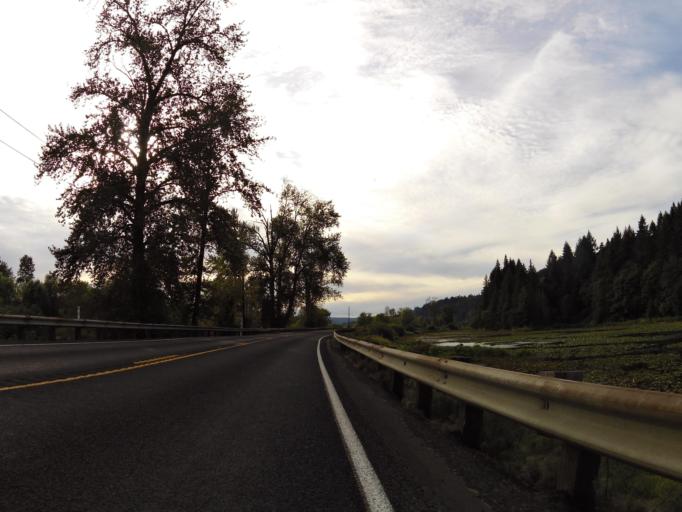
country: US
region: Washington
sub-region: Cowlitz County
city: West Longview
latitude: 46.1830
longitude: -123.0730
